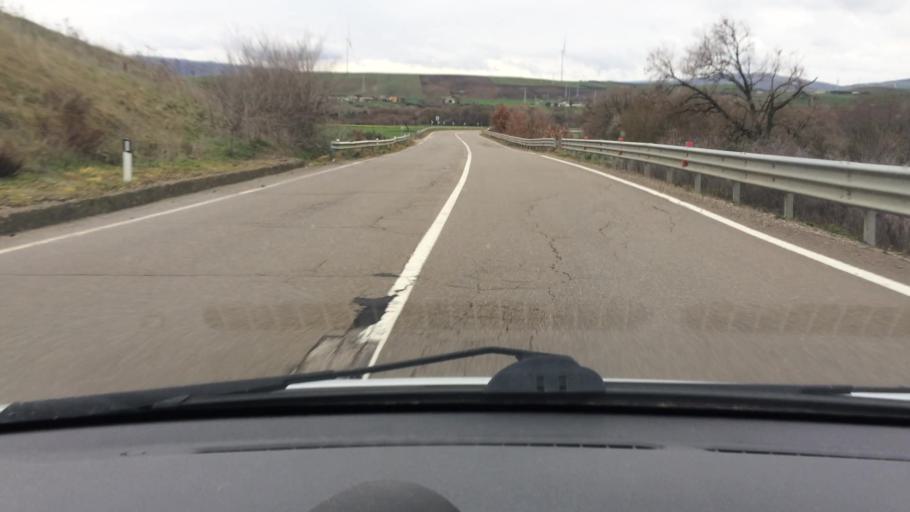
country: IT
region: Basilicate
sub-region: Provincia di Potenza
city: San Chirico Nuovo
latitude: 40.7735
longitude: 16.1217
